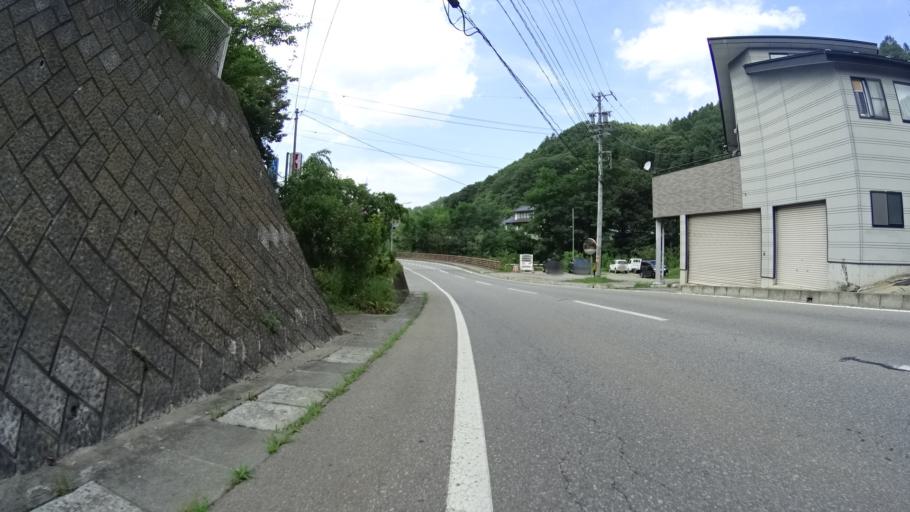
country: JP
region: Nagano
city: Saku
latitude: 36.0658
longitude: 138.5037
